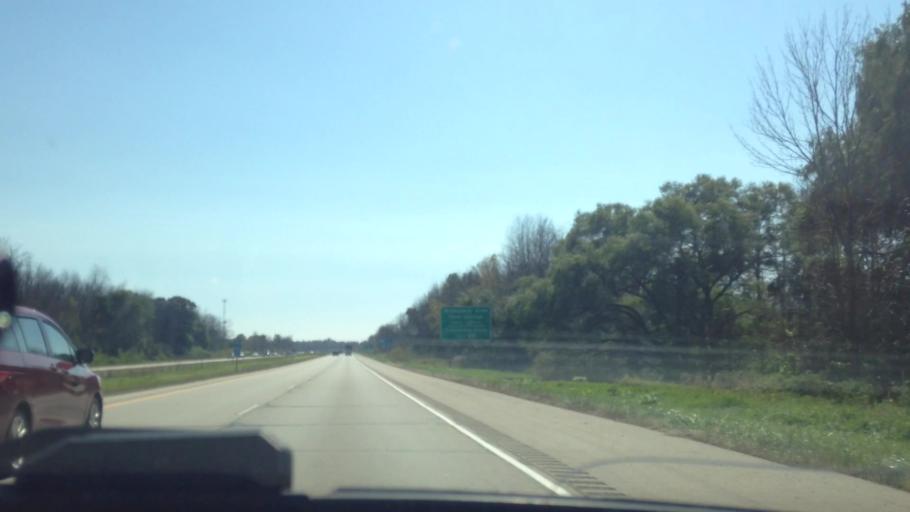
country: US
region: Wisconsin
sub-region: Ozaukee County
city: Grafton
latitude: 43.2911
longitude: -87.9210
